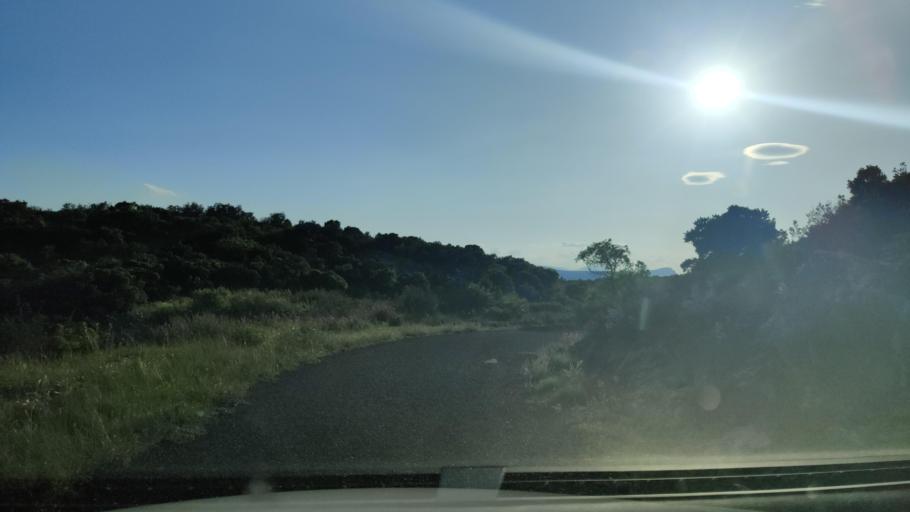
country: FR
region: Languedoc-Roussillon
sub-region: Departement des Pyrenees-Orientales
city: Estagel
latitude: 42.7914
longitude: 2.7335
